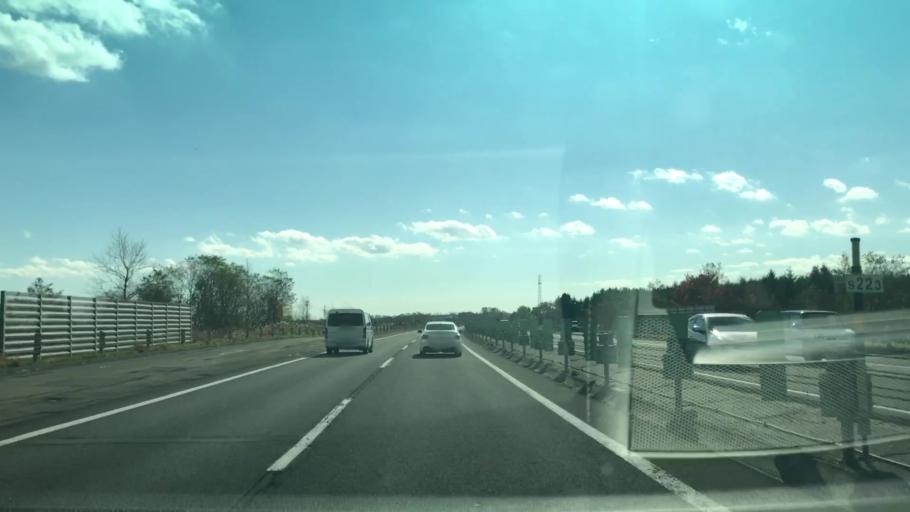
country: JP
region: Hokkaido
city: Kitahiroshima
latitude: 42.9066
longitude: 141.5507
